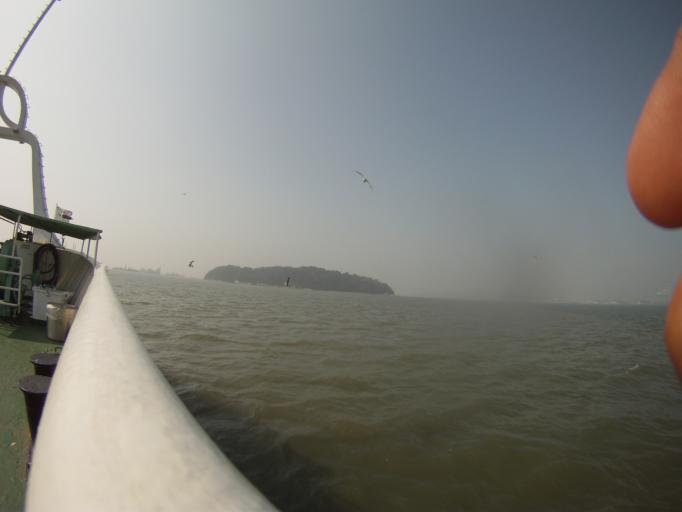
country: KR
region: Incheon
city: Incheon
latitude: 37.4953
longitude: 126.5818
